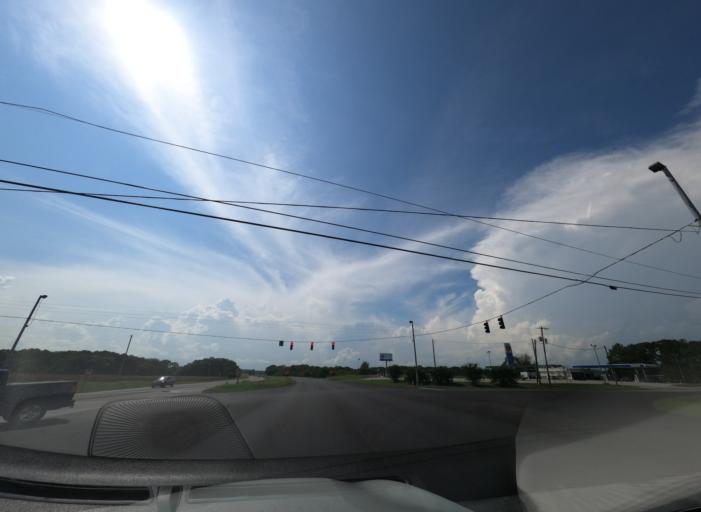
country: US
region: Alabama
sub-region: Lawrence County
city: Town Creek
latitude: 34.6852
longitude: -87.3087
